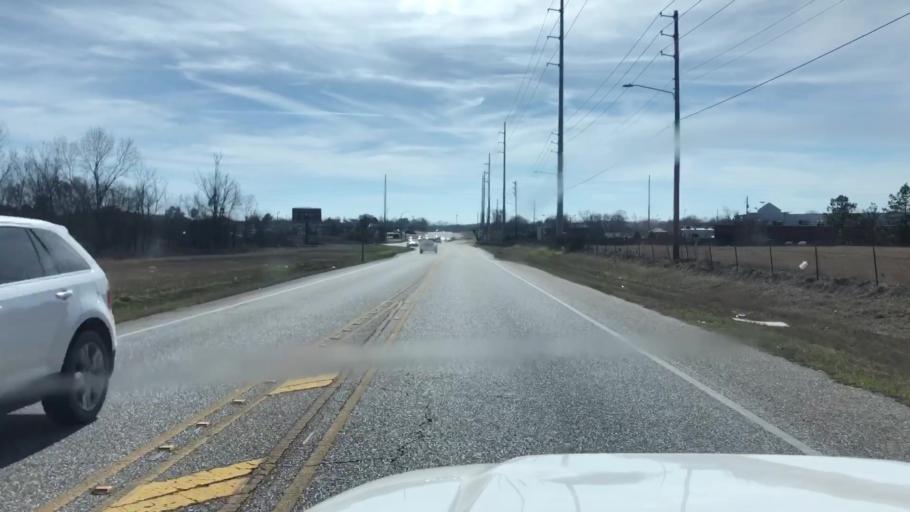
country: US
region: Alabama
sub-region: Elmore County
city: Blue Ridge
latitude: 32.3862
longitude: -86.1801
